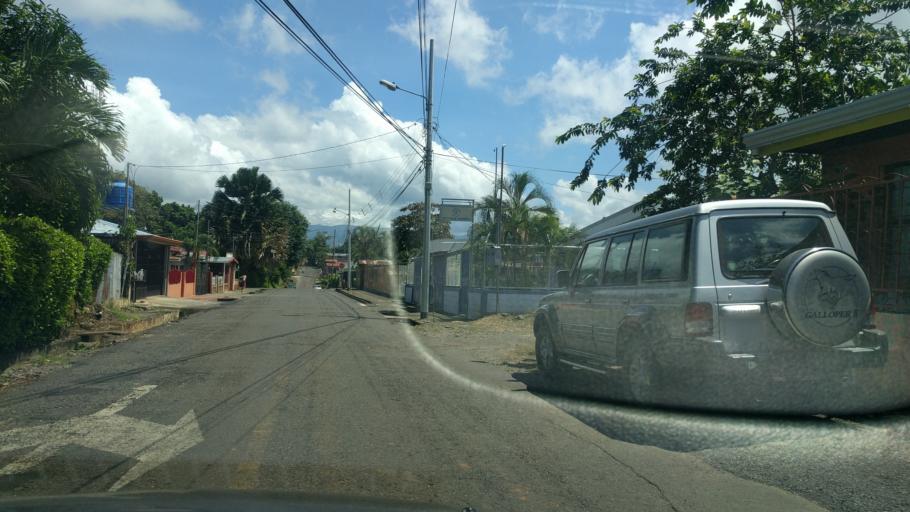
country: CR
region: Puntarenas
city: Esparza
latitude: 9.9905
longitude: -84.6641
